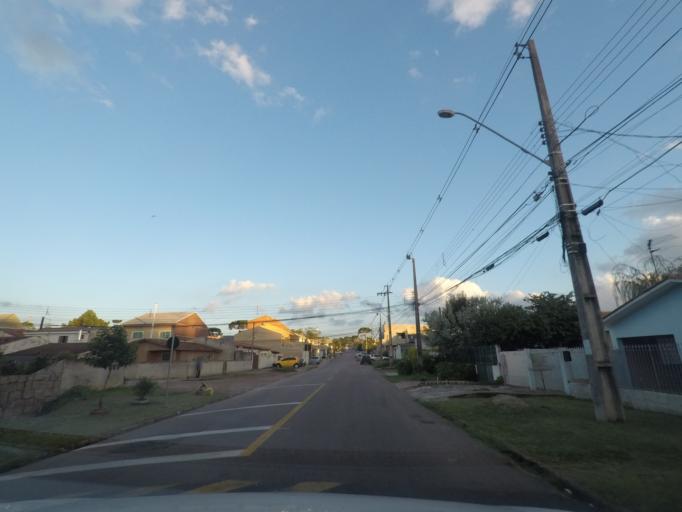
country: BR
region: Parana
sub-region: Sao Jose Dos Pinhais
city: Sao Jose dos Pinhais
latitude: -25.4965
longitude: -49.2567
